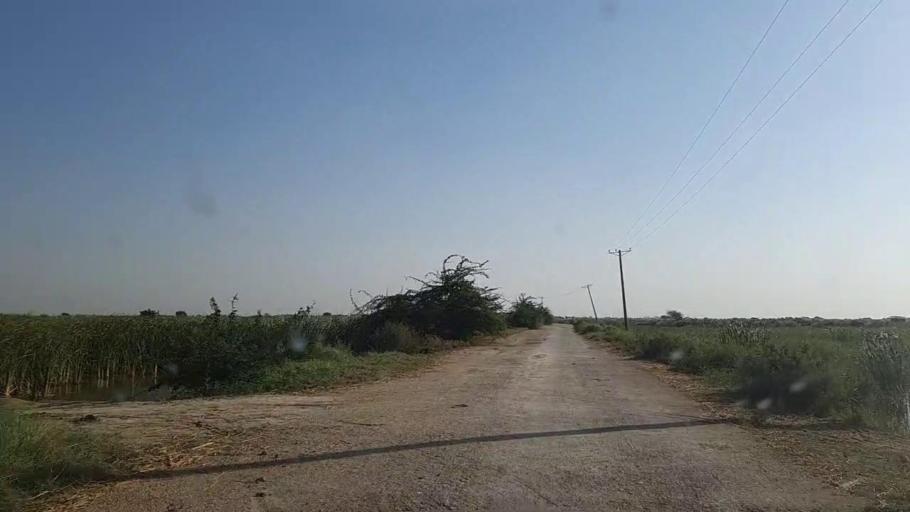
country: PK
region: Sindh
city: Thatta
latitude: 24.6429
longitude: 68.0752
